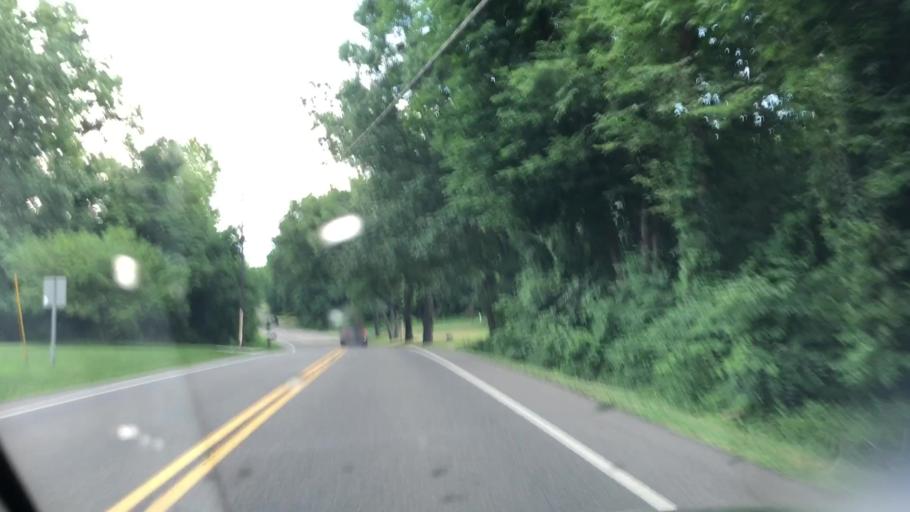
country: US
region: Ohio
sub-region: Summit County
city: Portage Lakes
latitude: 40.9884
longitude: -81.5488
